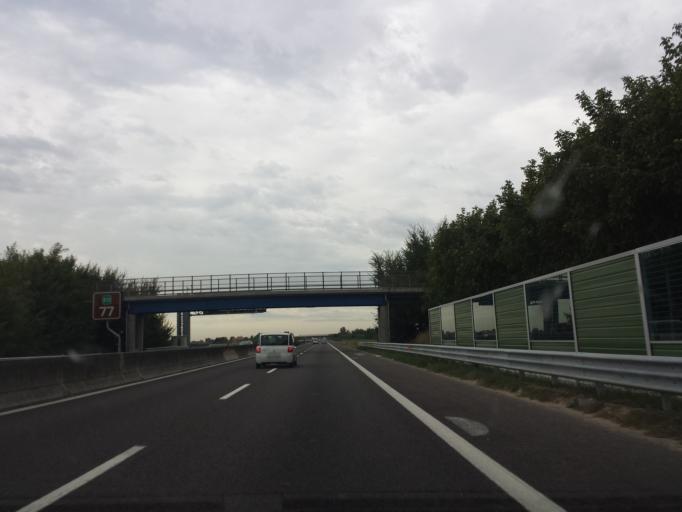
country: IT
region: Veneto
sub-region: Provincia di Padova
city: Monselice
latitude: 45.2217
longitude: 11.7746
